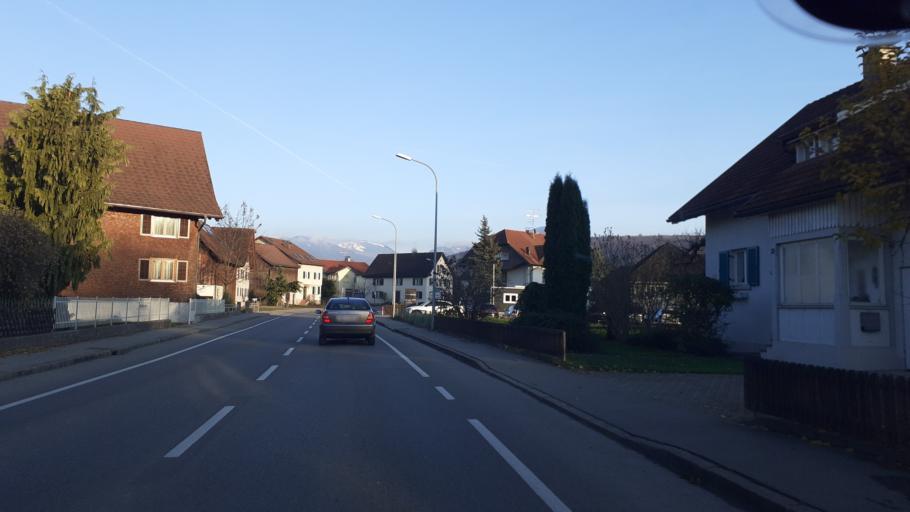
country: AT
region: Vorarlberg
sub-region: Politischer Bezirk Feldkirch
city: Nofels
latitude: 47.2551
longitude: 9.5741
